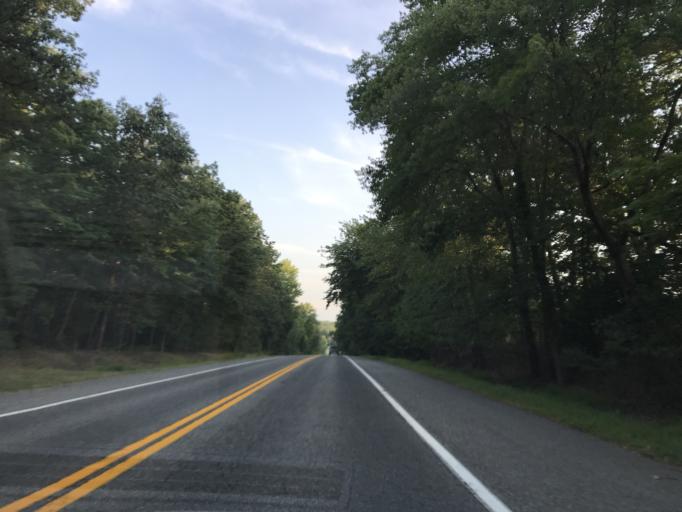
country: US
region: Maryland
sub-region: Cecil County
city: Charlestown
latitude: 39.5261
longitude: -75.9539
